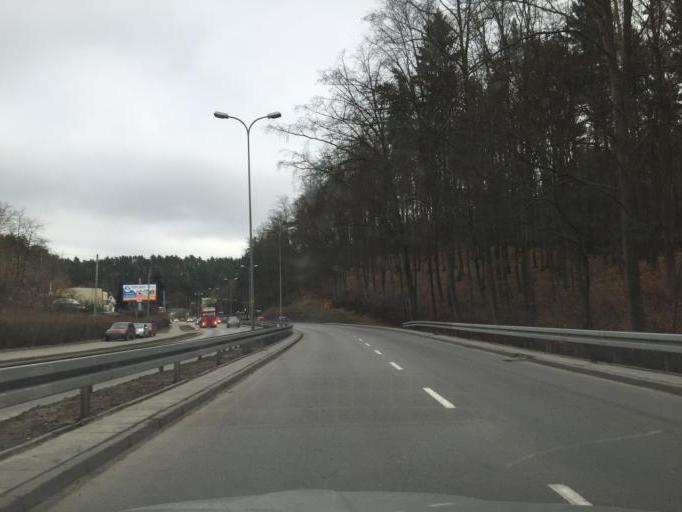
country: PL
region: Pomeranian Voivodeship
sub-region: Powiat gdanski
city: Kowale
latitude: 54.3718
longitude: 18.5533
